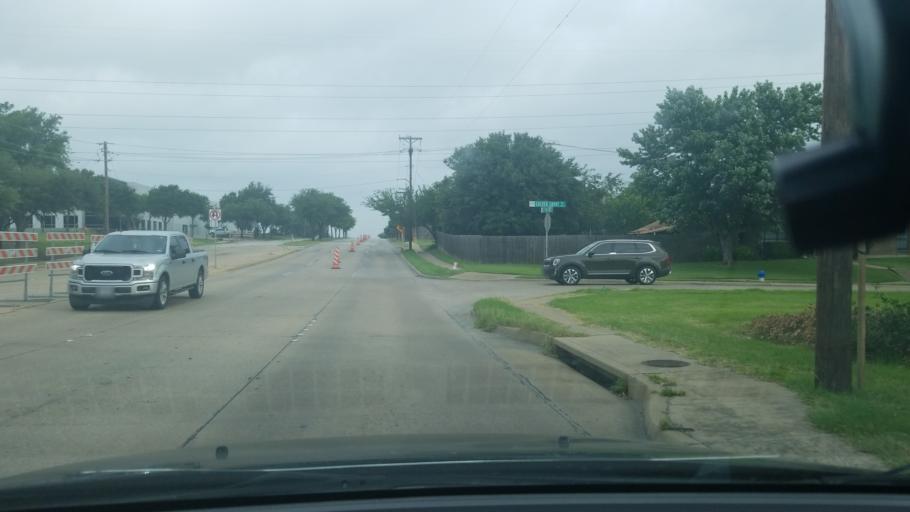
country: US
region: Texas
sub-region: Dallas County
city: Mesquite
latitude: 32.7834
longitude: -96.6480
